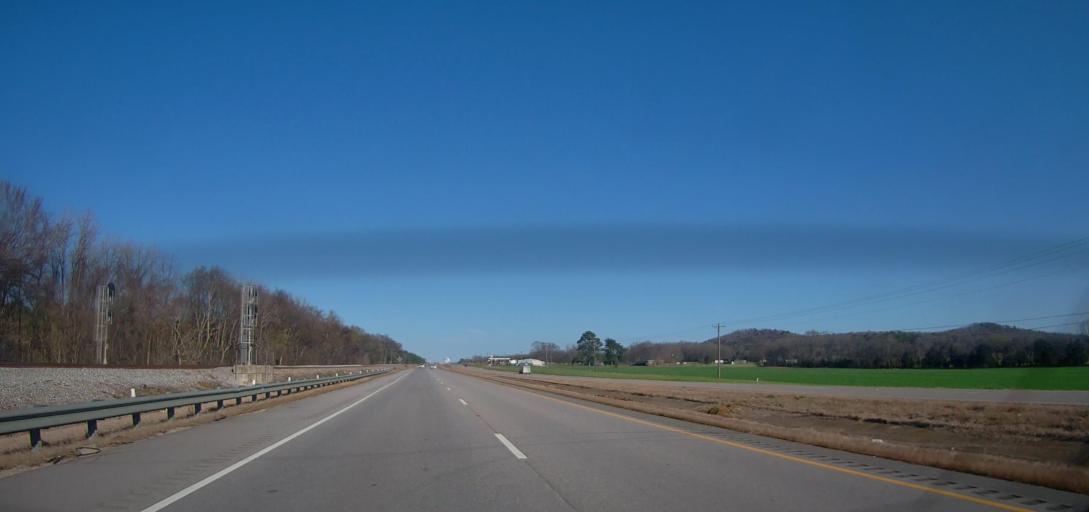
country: US
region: Alabama
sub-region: Colbert County
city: Cherokee
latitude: 34.7292
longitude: -87.8448
